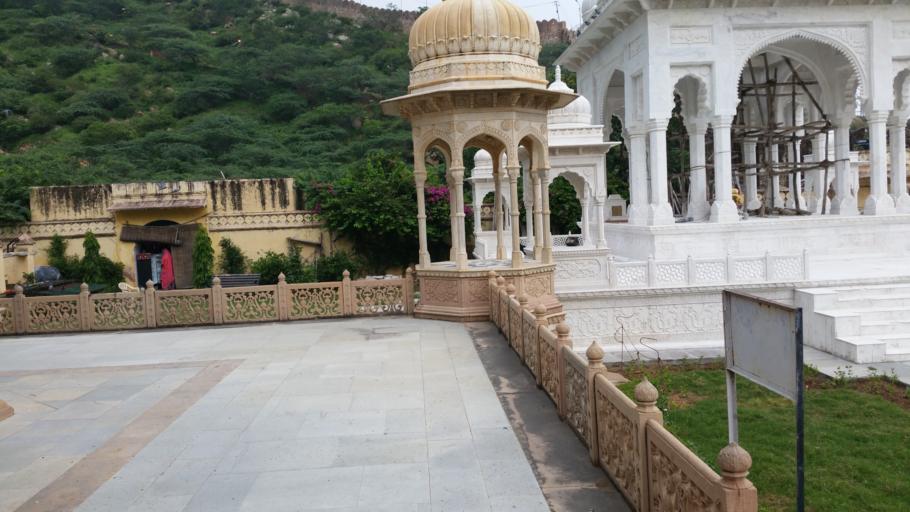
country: IN
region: Rajasthan
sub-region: Jaipur
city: Jaipur
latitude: 26.9428
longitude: 75.8247
